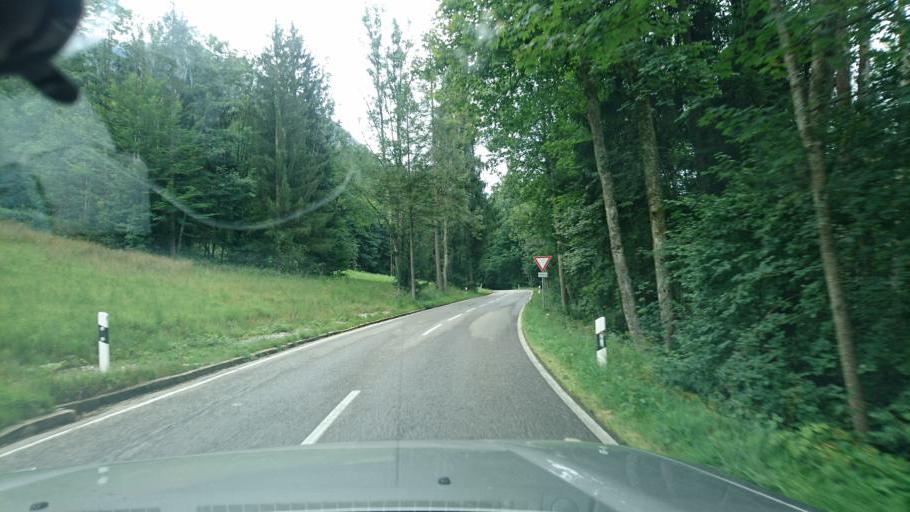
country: DE
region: Bavaria
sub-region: Upper Bavaria
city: Ruhpolding
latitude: 47.7495
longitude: 12.6748
